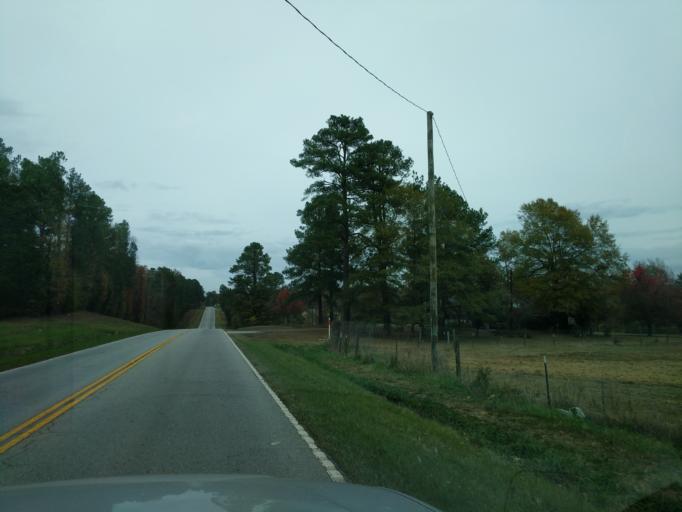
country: US
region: South Carolina
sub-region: Saluda County
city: Saluda
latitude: 34.0682
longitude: -81.7611
